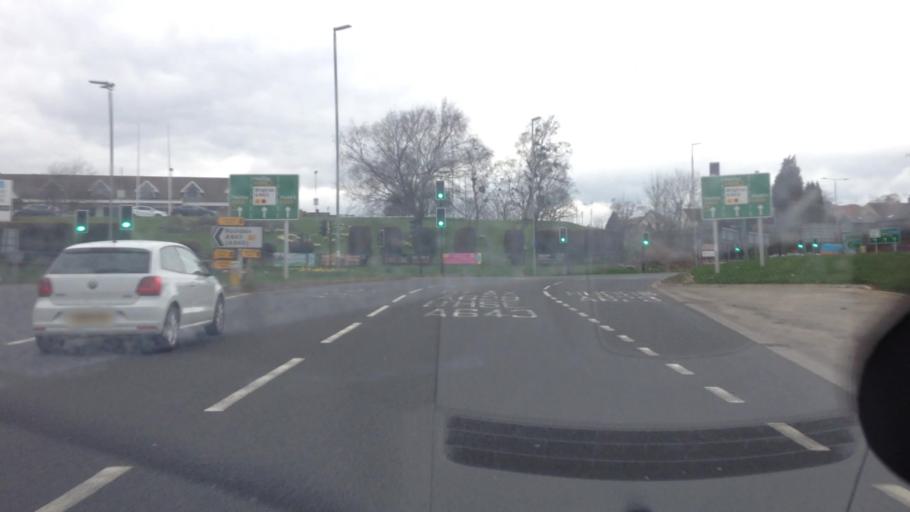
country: GB
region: England
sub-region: Calderdale
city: Elland
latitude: 53.6693
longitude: -1.8274
